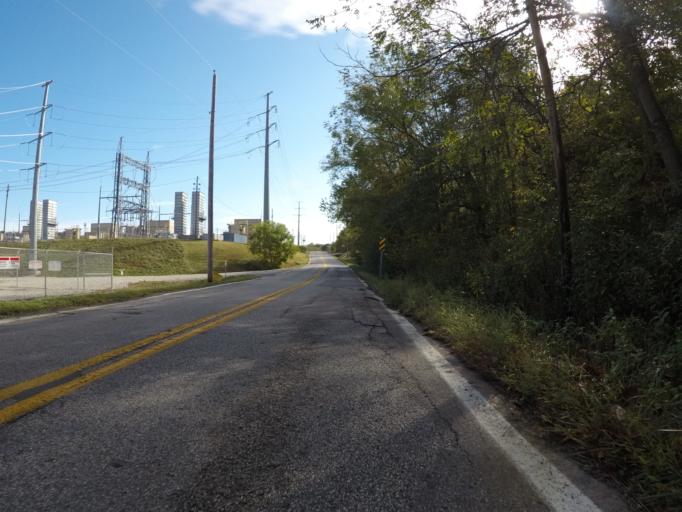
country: US
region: West Virginia
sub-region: Wayne County
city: Ceredo
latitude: 38.3671
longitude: -82.5358
